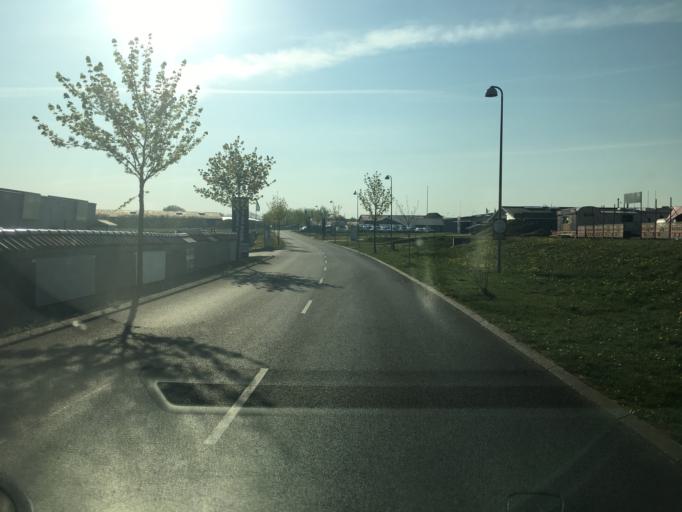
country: DK
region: South Denmark
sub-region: Aabenraa Kommune
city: Rodekro
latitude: 55.0721
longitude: 9.3495
